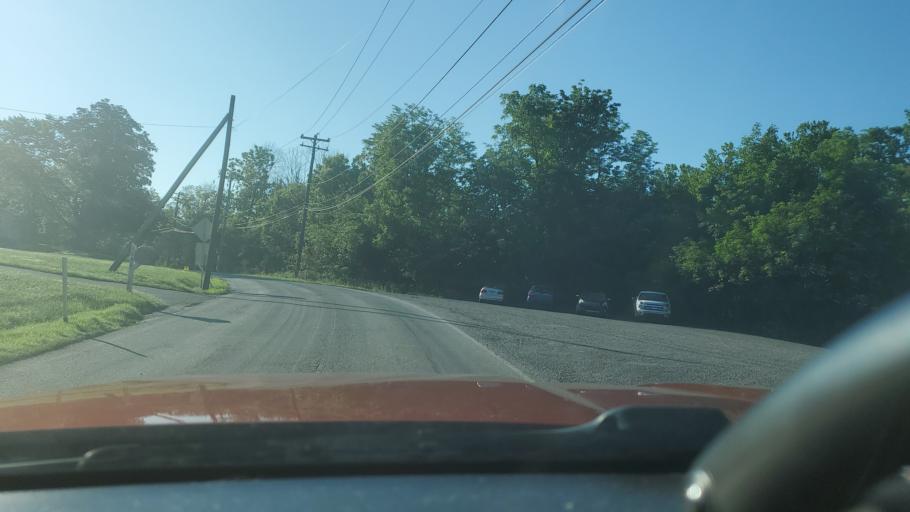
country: US
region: Pennsylvania
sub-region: Montgomery County
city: Woxall
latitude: 40.3227
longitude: -75.4765
